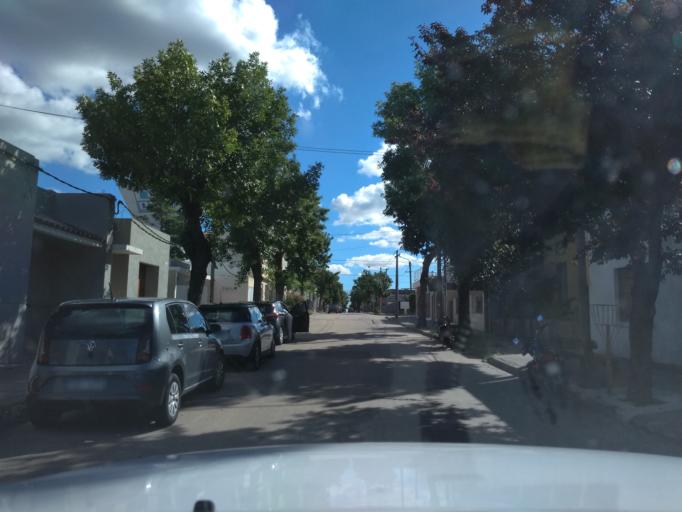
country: UY
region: Florida
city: Florida
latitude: -34.0954
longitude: -56.2136
